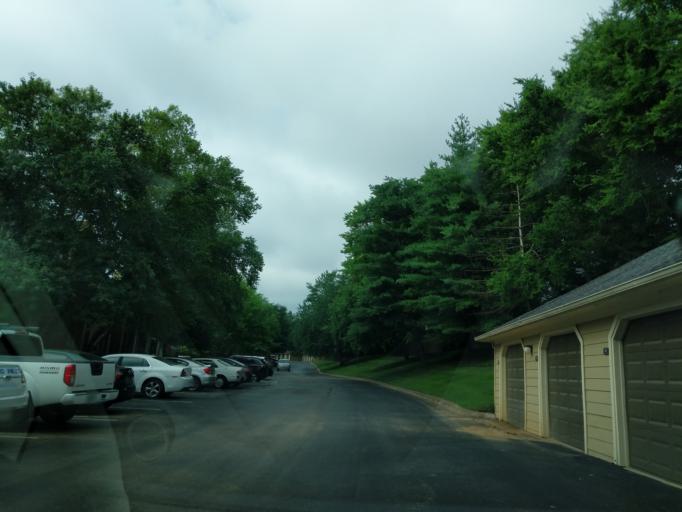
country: US
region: Tennessee
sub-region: Davidson County
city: Lakewood
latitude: 36.1722
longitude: -86.6131
